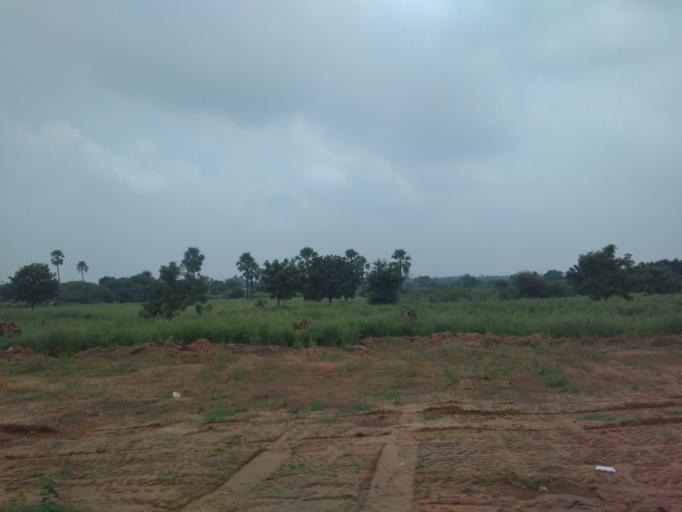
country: IN
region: Telangana
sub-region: Warangal
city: Jangaon
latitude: 17.6803
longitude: 79.1058
